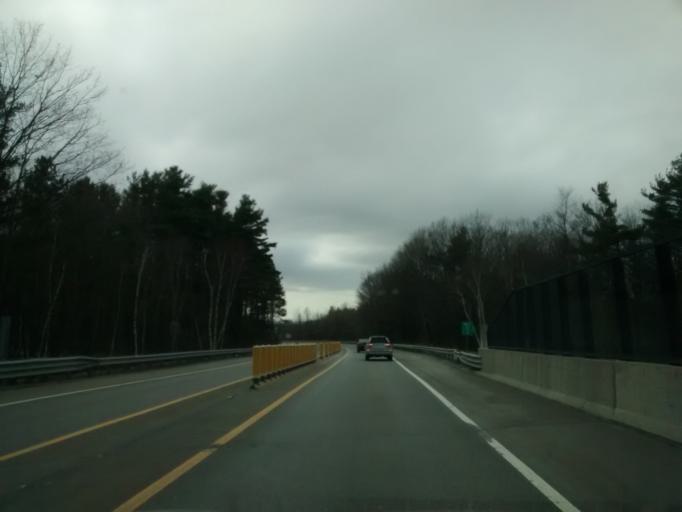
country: US
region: Massachusetts
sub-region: Worcester County
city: Phillipston
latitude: 42.5765
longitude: -72.1704
